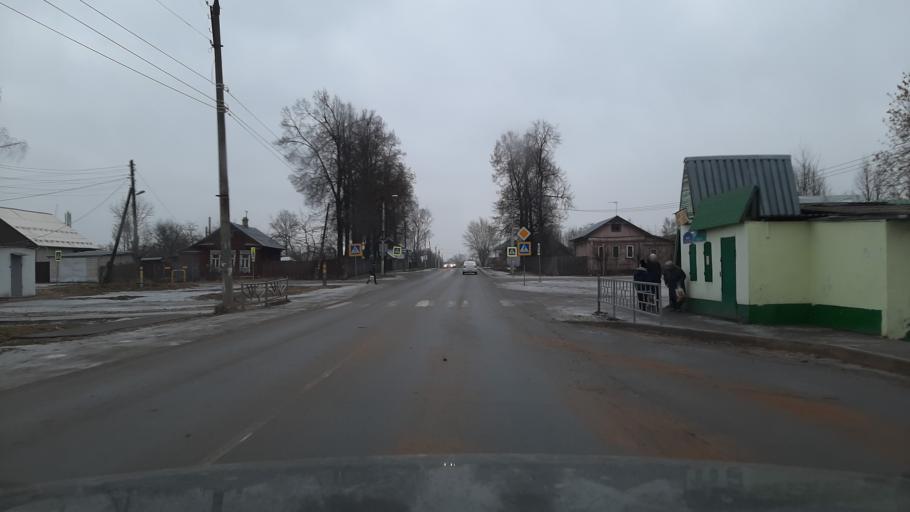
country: RU
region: Ivanovo
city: Shuya
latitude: 56.8628
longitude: 41.3651
